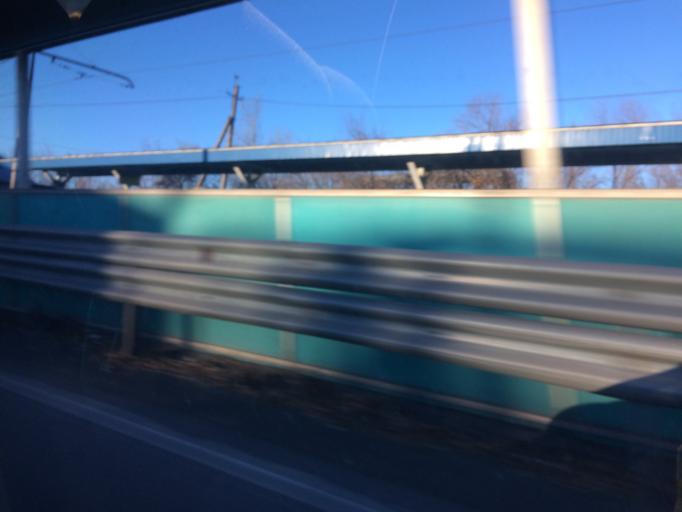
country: RU
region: Chelyabinsk
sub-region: Gorod Magnitogorsk
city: Magnitogorsk
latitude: 53.4027
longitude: 59.0266
